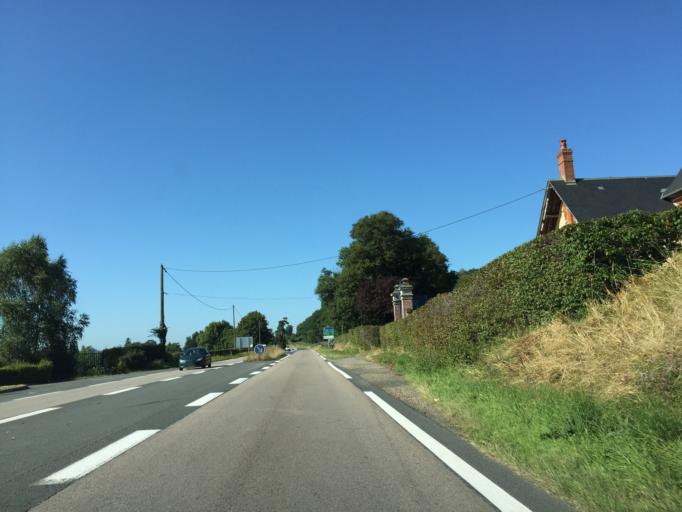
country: FR
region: Lower Normandy
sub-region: Departement du Calvados
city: Lisieux
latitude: 49.1651
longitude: 0.2278
